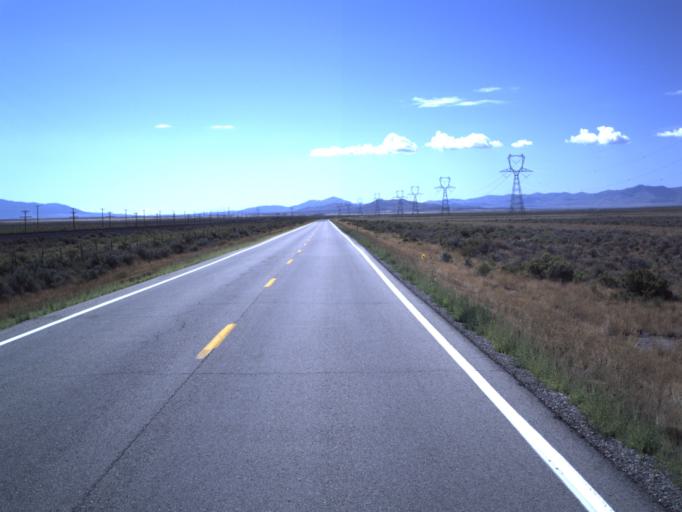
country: US
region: Utah
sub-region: Tooele County
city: Tooele
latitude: 40.2859
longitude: -112.3997
